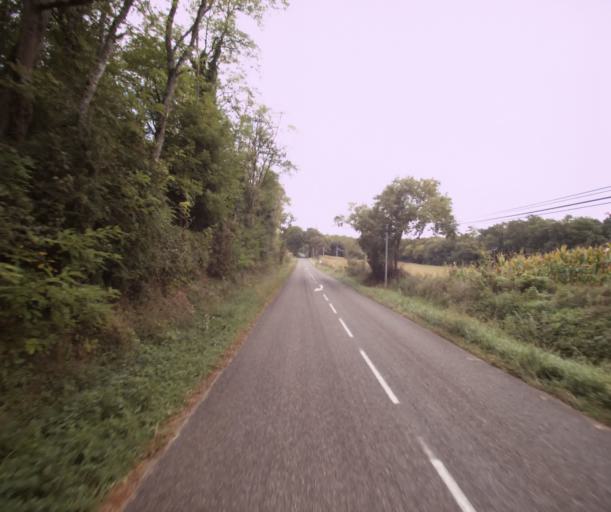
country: FR
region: Midi-Pyrenees
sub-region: Departement du Gers
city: Cazaubon
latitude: 43.8672
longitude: -0.0898
